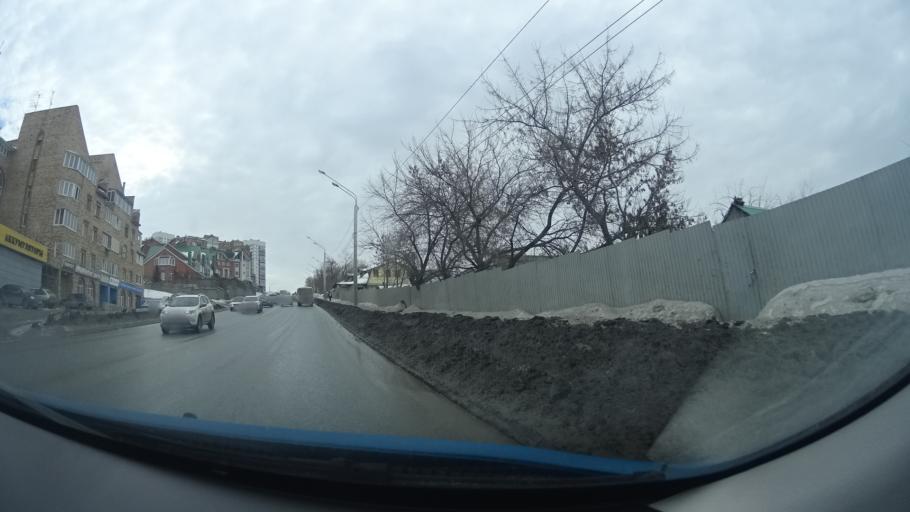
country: RU
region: Bashkortostan
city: Ufa
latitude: 54.7047
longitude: 55.9745
